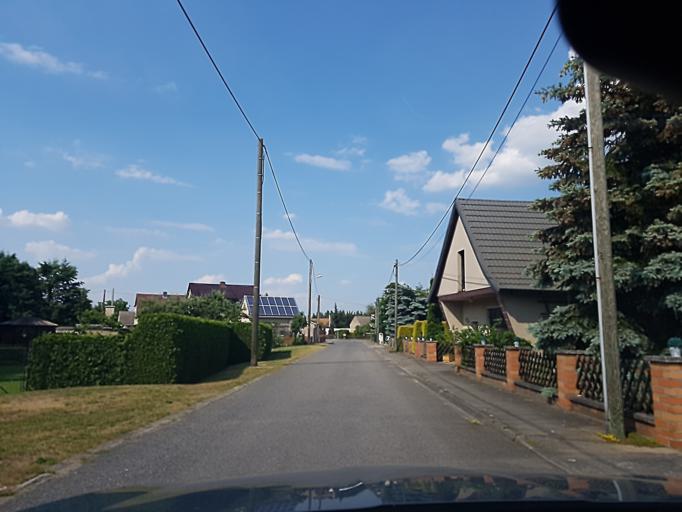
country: DE
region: Brandenburg
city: Schonborn
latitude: 51.5411
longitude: 13.4649
